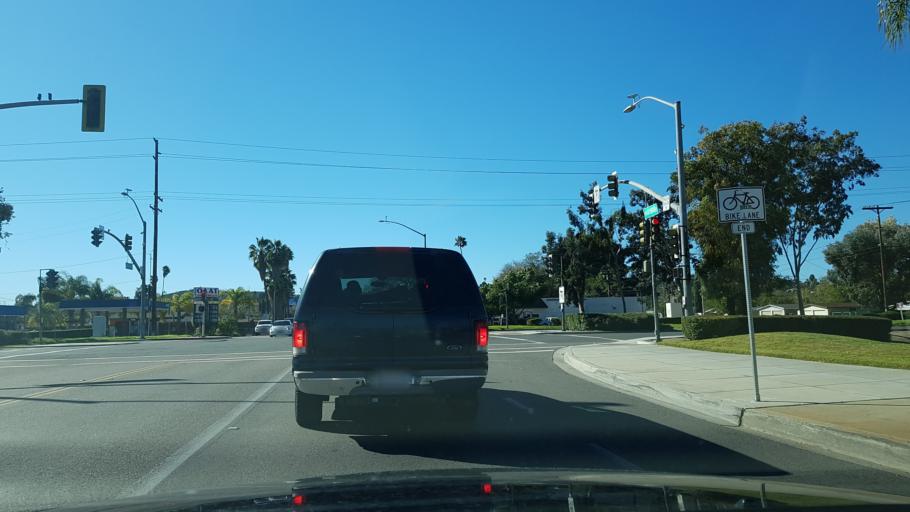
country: US
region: California
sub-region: San Diego County
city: Escondido
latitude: 33.1121
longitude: -117.0812
